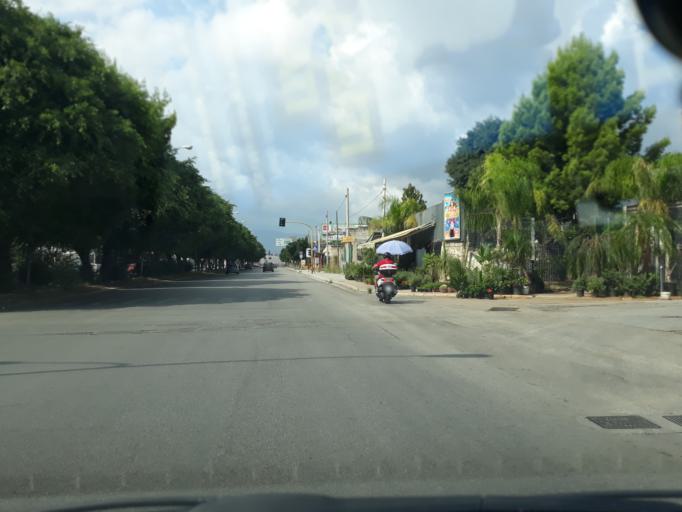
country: IT
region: Sicily
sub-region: Palermo
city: Palermo
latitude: 38.0970
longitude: 13.3447
